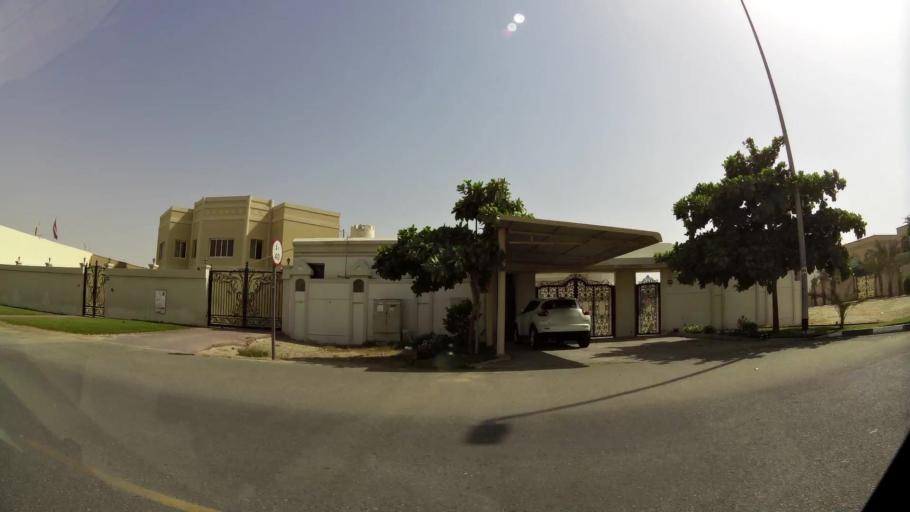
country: AE
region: Dubai
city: Dubai
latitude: 25.1608
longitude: 55.2546
